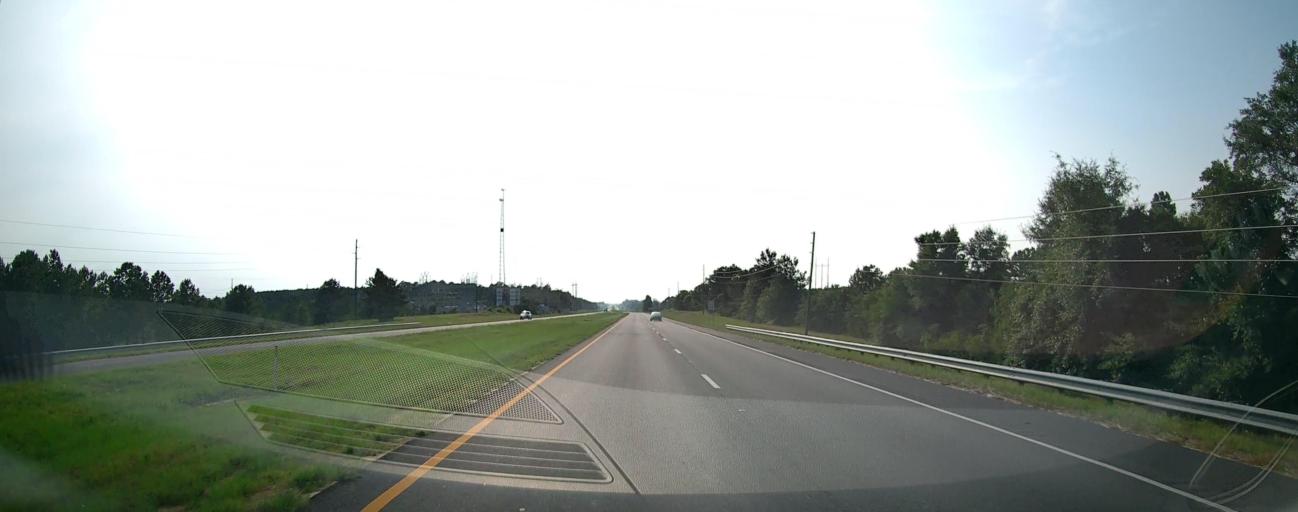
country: US
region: Georgia
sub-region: Taylor County
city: Butler
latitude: 32.5707
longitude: -84.2855
